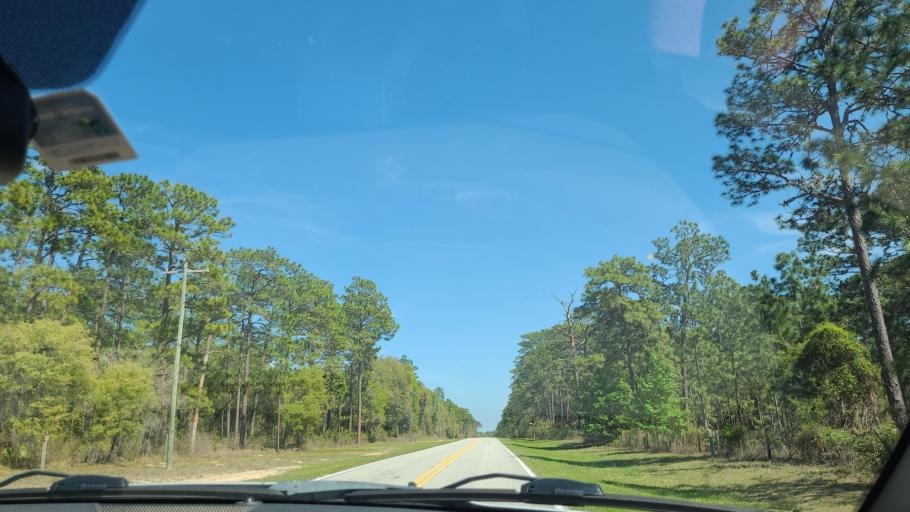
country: US
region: Florida
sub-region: Putnam County
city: Interlachen
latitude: 29.3780
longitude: -81.7885
